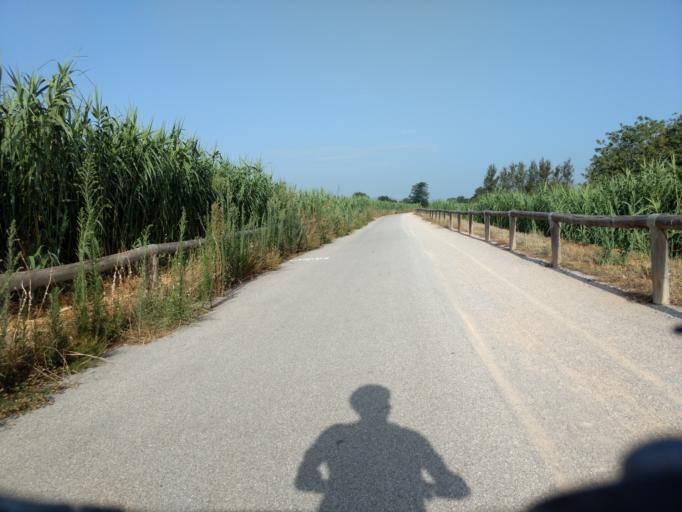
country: FR
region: Languedoc-Roussillon
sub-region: Departement des Pyrenees-Orientales
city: Pia
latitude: 42.7603
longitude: 2.9287
